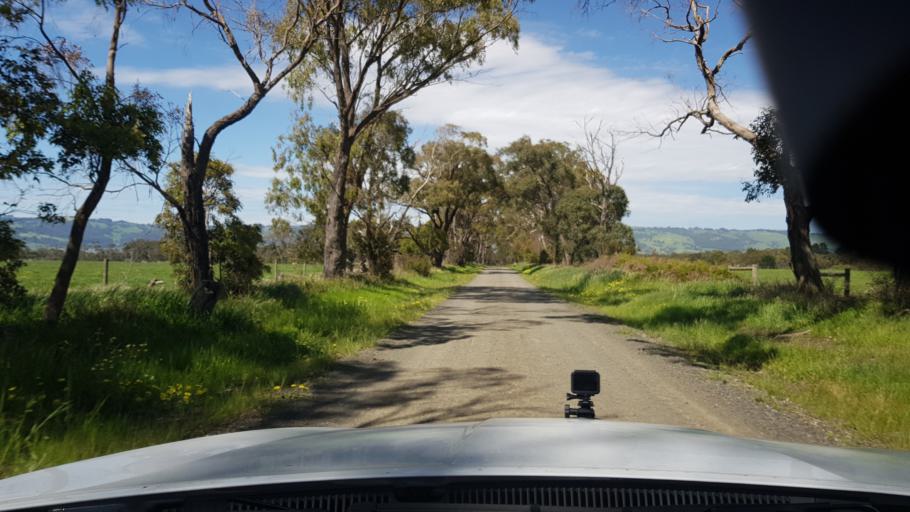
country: AU
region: Victoria
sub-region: Latrobe
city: Moe
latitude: -38.1580
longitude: 146.1360
